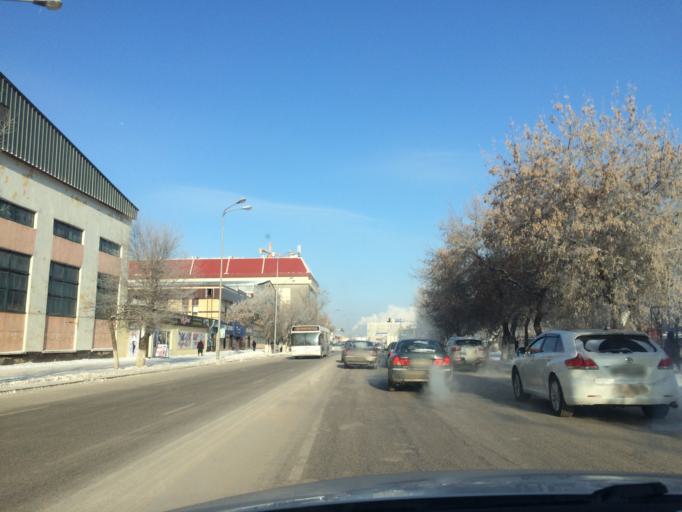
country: KZ
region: Astana Qalasy
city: Astana
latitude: 51.1715
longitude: 71.4386
